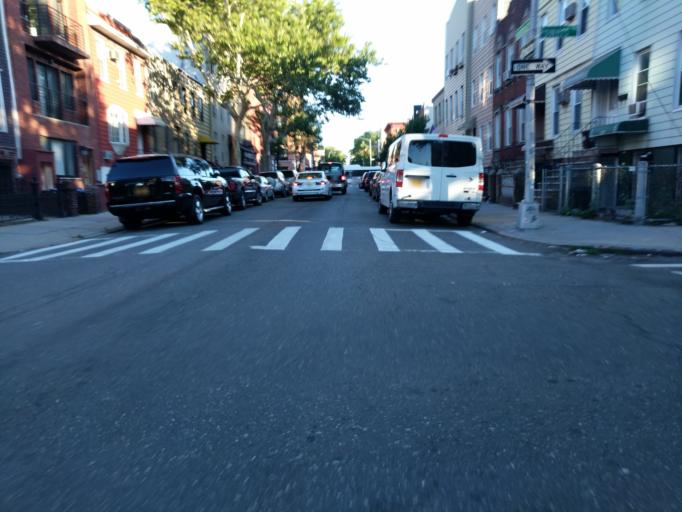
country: US
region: New York
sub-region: Queens County
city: Long Island City
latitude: 40.7126
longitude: -73.9424
